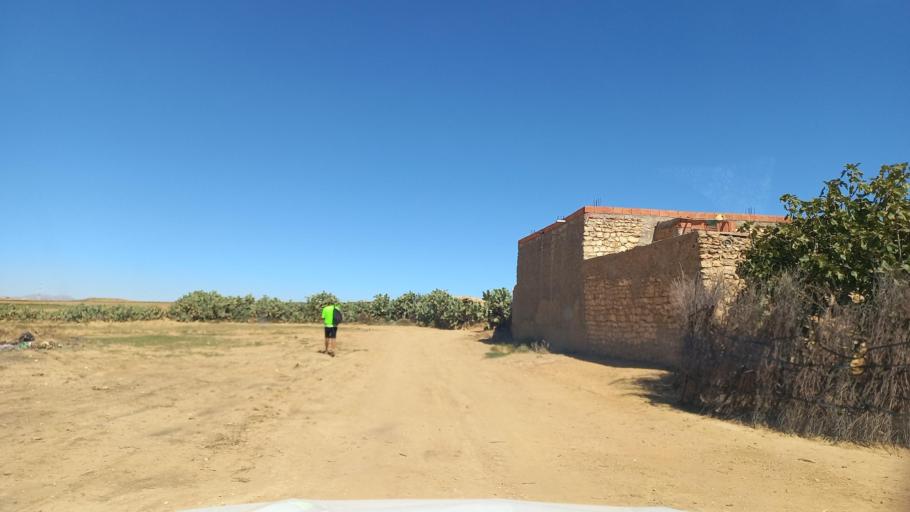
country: TN
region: Al Qasrayn
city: Sbiba
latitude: 35.3507
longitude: 9.1020
